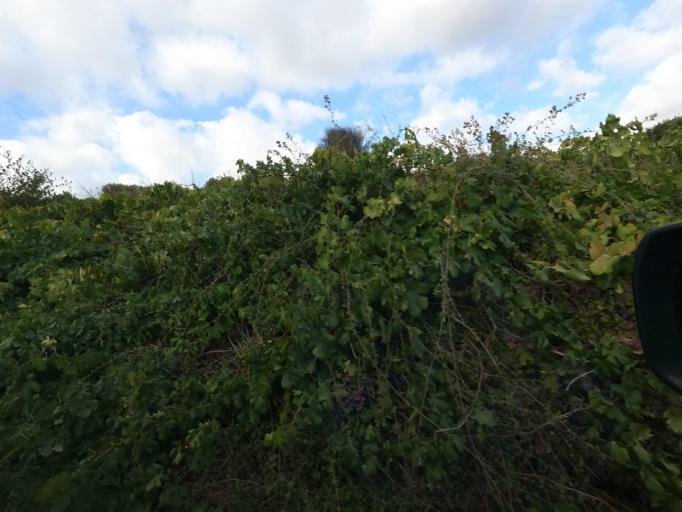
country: CY
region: Pafos
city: Mesogi
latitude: 34.8489
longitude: 32.5377
